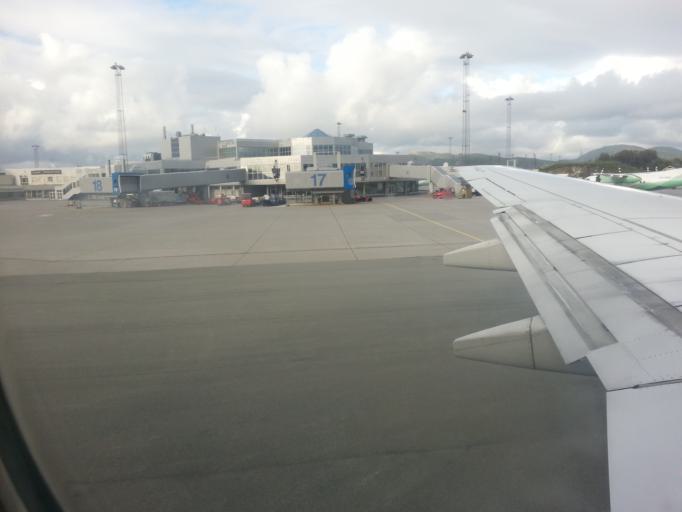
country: NO
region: Nordland
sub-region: Bodo
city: Bodo
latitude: 67.2710
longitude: 14.3674
